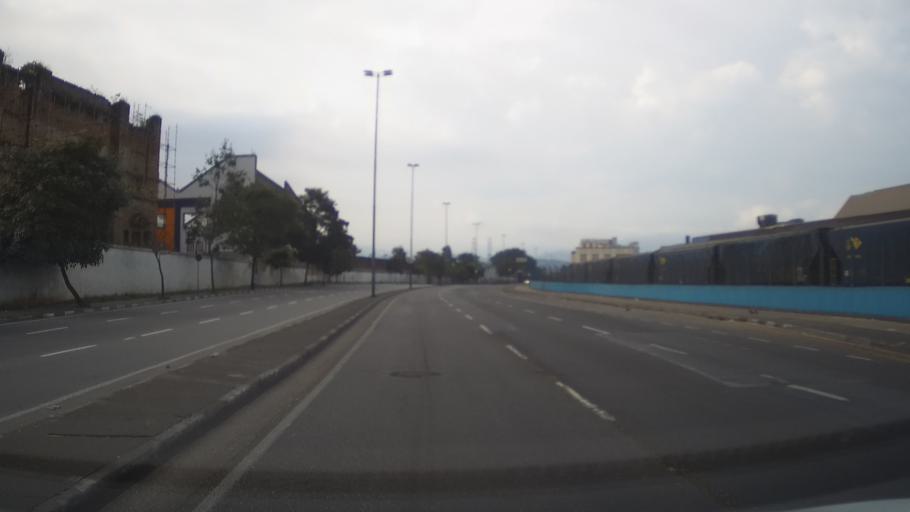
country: BR
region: Sao Paulo
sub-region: Santos
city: Santos
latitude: -23.9460
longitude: -46.3176
